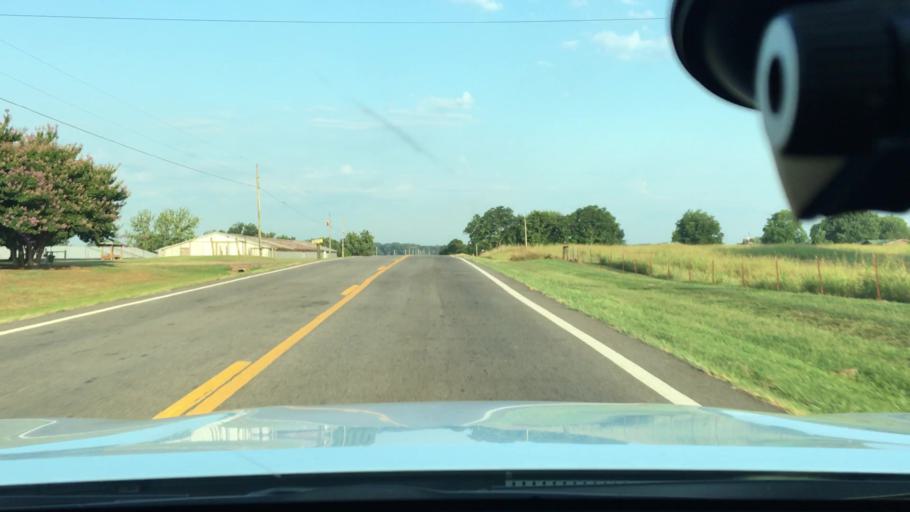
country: US
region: Arkansas
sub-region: Johnson County
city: Clarksville
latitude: 35.3789
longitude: -93.5438
